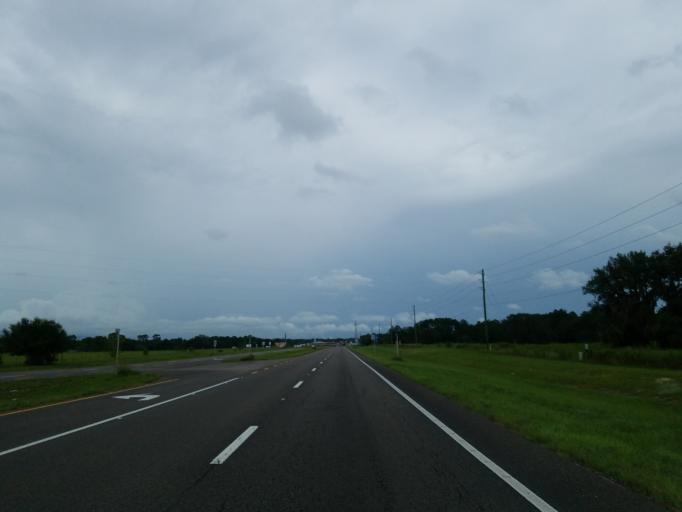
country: US
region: Florida
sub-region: Sumter County
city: Wildwood
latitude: 28.8773
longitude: -82.1079
